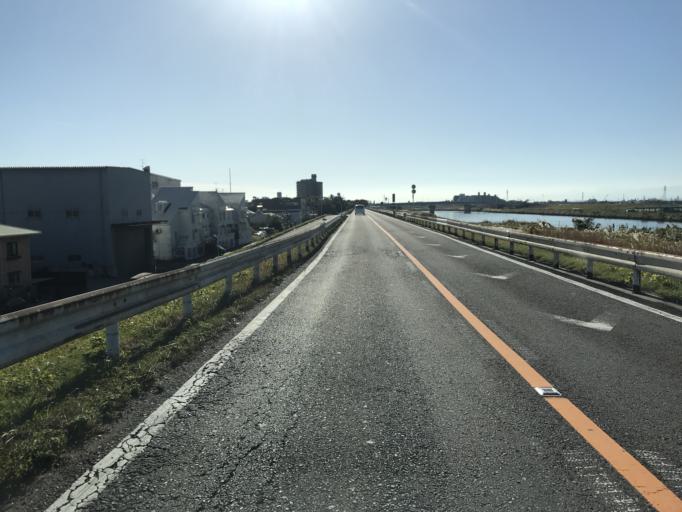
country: JP
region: Aichi
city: Kanie
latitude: 35.1737
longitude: 136.8421
